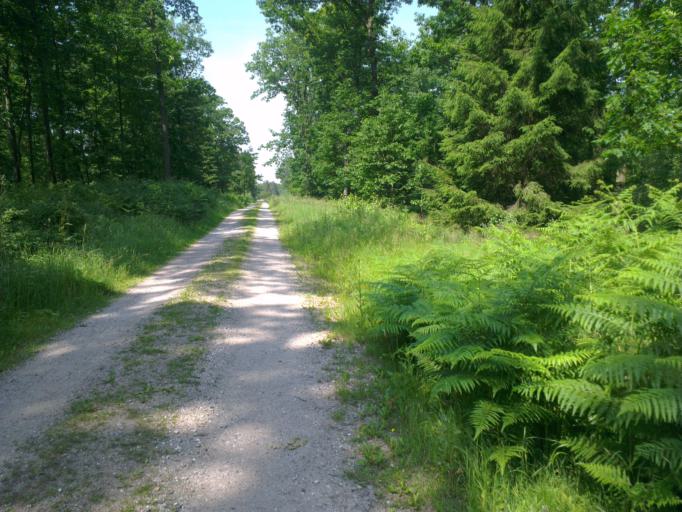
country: DK
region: Capital Region
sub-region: Allerod Kommune
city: Lillerod
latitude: 55.9125
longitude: 12.3608
